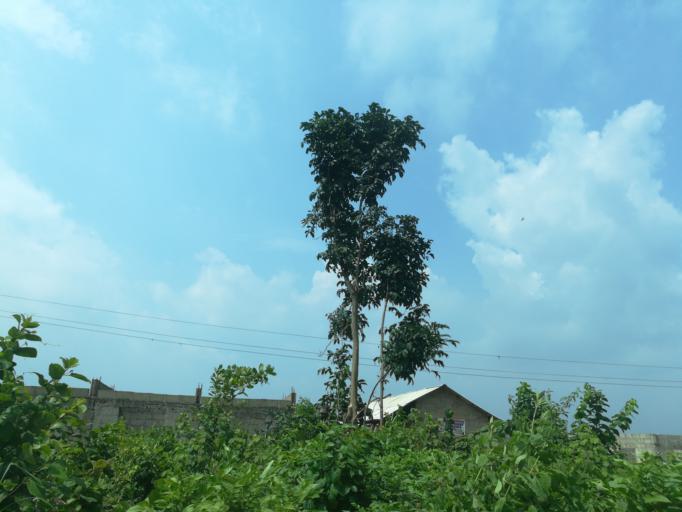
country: NG
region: Lagos
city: Ikorodu
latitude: 6.5936
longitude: 3.6386
